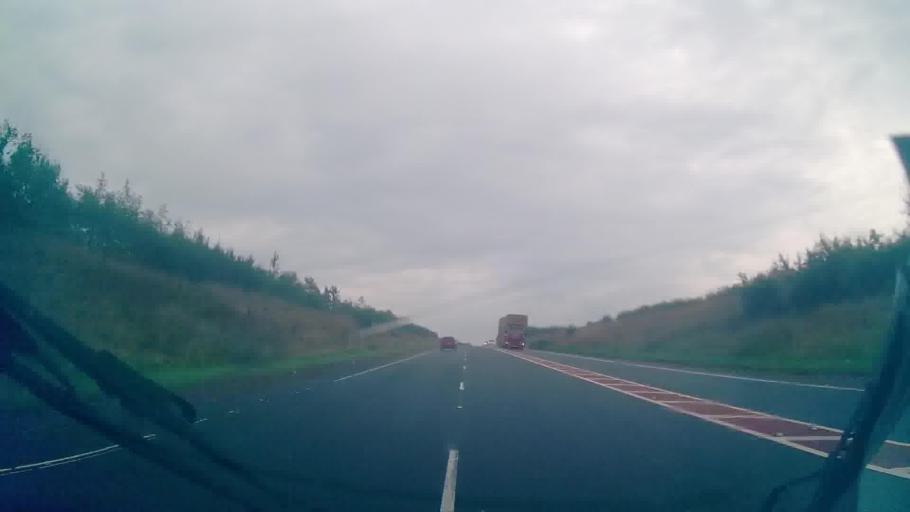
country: GB
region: Scotland
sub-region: Dumfries and Galloway
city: Lockerbie
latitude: 55.0246
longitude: -3.3795
